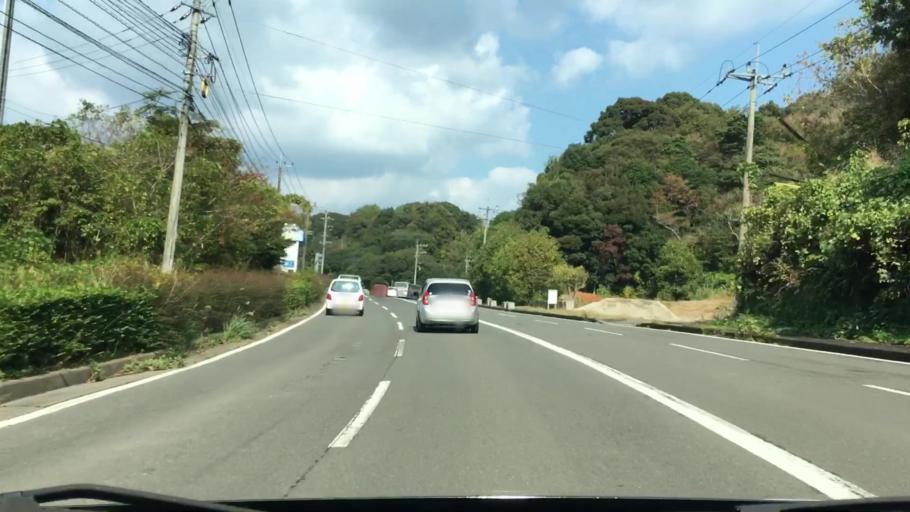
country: JP
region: Nagasaki
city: Sasebo
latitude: 32.9895
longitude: 129.7489
